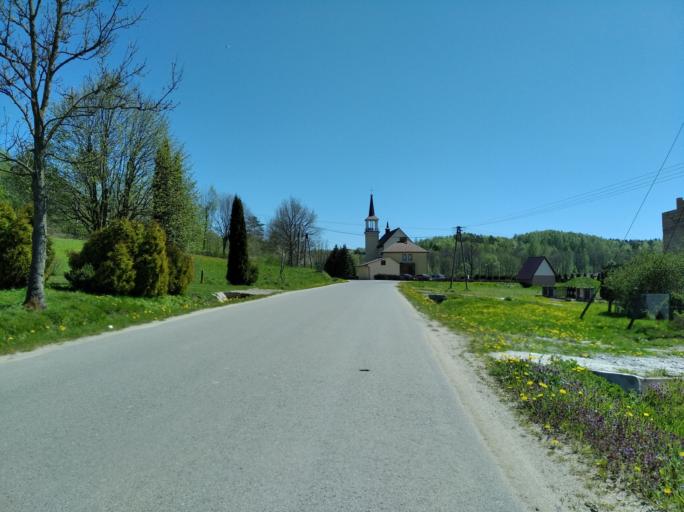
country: PL
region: Subcarpathian Voivodeship
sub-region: Powiat debicki
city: Brzostek
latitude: 49.8967
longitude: 21.4863
